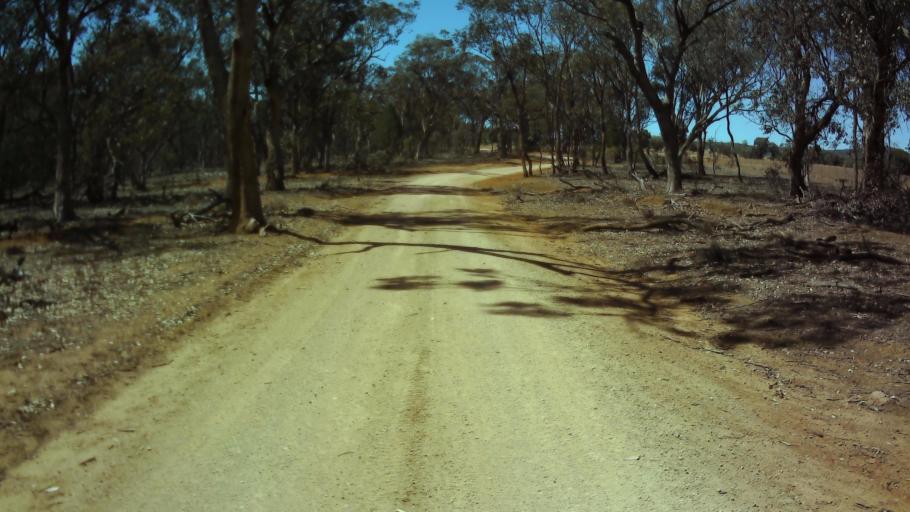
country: AU
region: New South Wales
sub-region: Weddin
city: Grenfell
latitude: -33.9415
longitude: 148.0785
